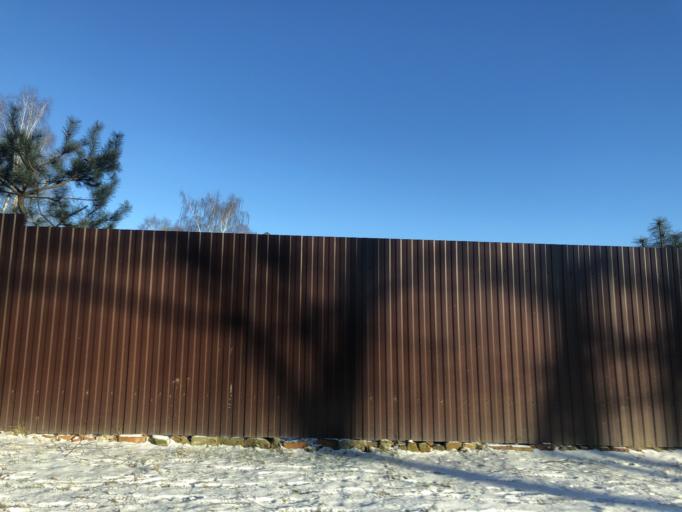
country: RU
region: Tverskaya
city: Rzhev
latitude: 56.2819
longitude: 34.3207
